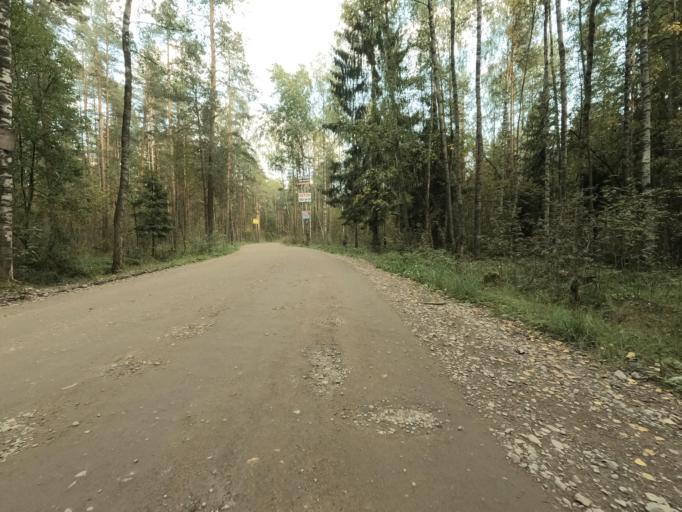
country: RU
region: Leningrad
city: Imeni Sverdlova
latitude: 59.8413
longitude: 30.6944
